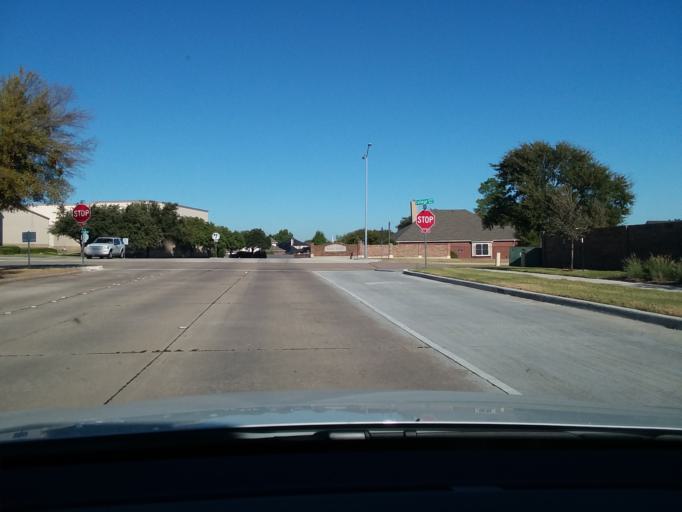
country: US
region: Texas
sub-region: Denton County
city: Lewisville
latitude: 33.0506
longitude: -97.0174
